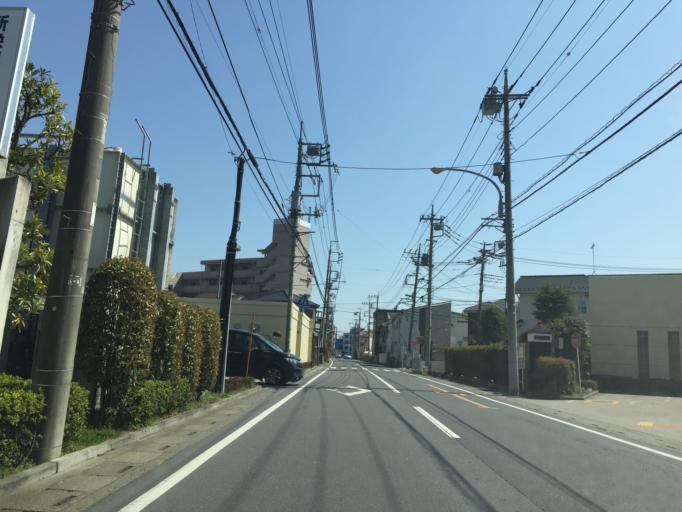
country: JP
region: Saitama
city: Yono
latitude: 35.8507
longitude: 139.6291
